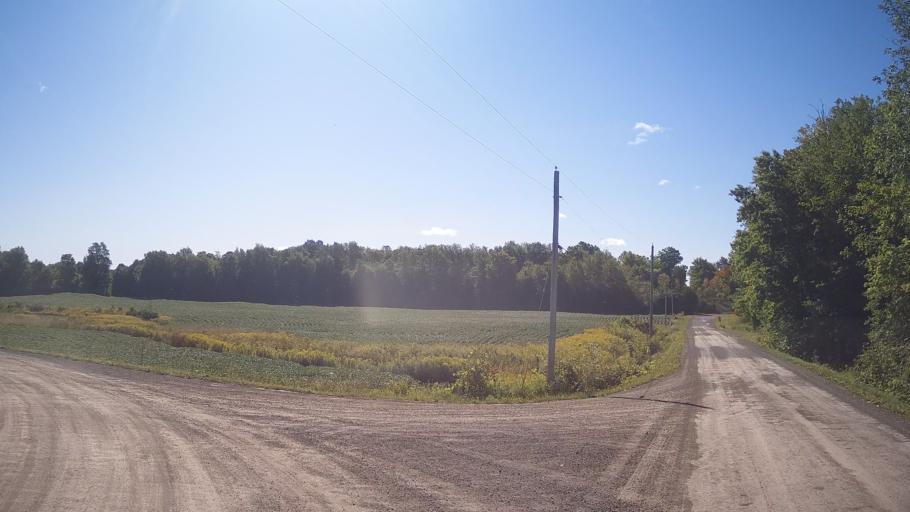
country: CA
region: Ontario
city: Prescott
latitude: 44.9705
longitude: -75.5659
